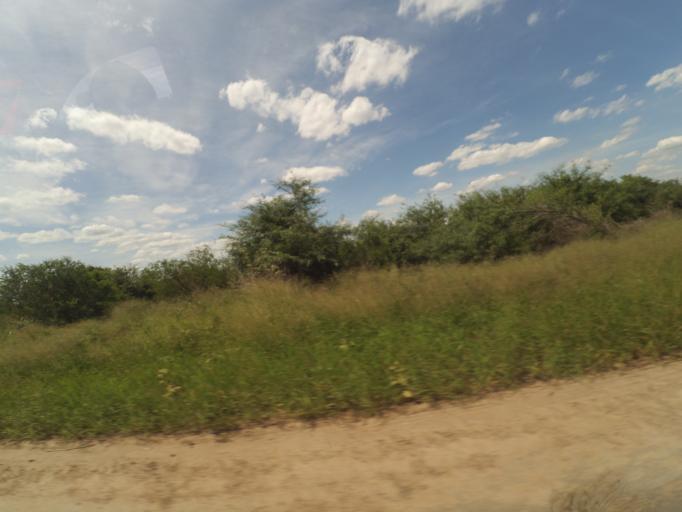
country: BO
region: Santa Cruz
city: Pailon
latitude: -17.5895
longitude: -61.9707
